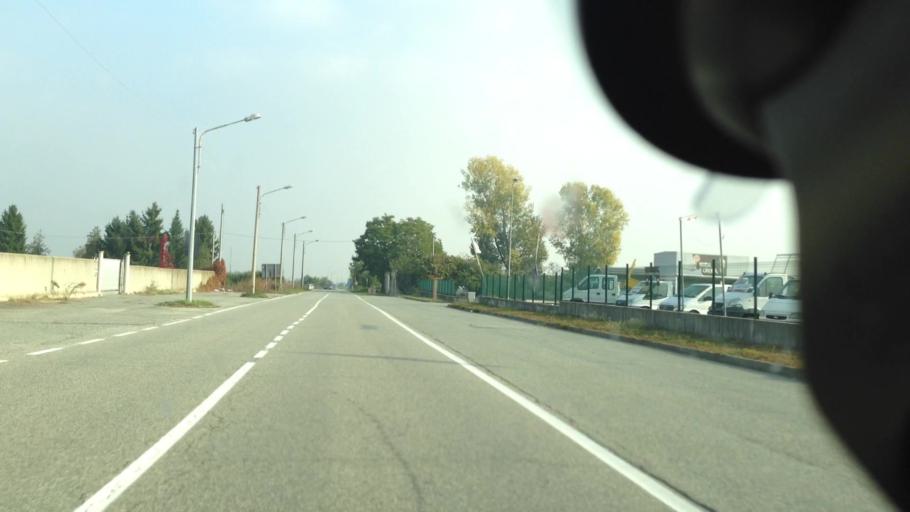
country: IT
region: Piedmont
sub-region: Provincia di Vercelli
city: Cigliano
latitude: 45.3024
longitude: 8.0329
